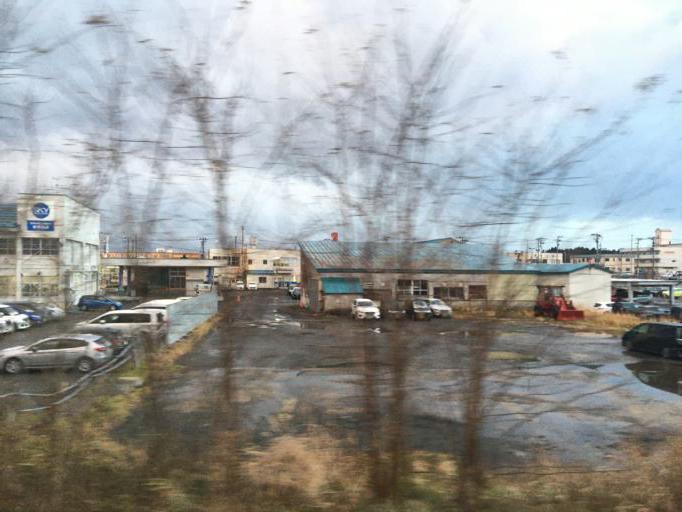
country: JP
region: Aomori
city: Aomori Shi
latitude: 40.8266
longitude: 140.7063
